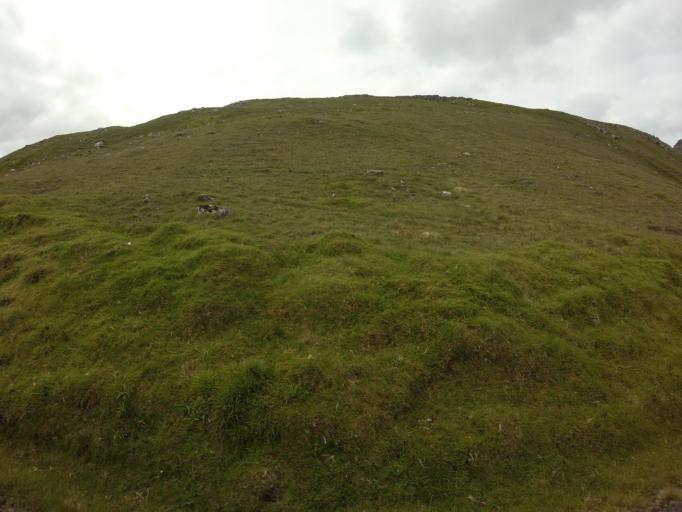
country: FO
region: Suduroy
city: Tvoroyri
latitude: 61.5249
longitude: -6.8274
